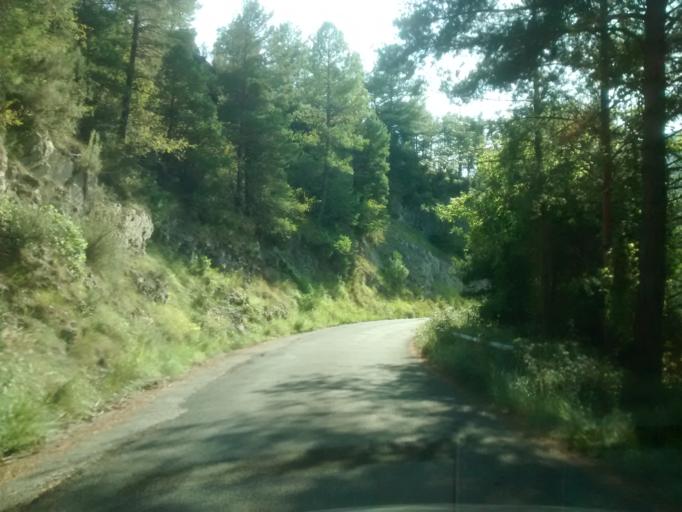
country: ES
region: Aragon
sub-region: Provincia de Huesca
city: Puertolas
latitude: 42.5497
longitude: 0.1675
